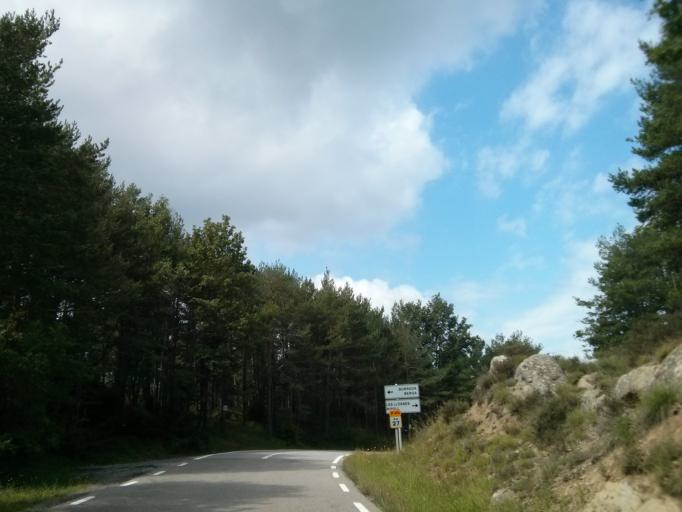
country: ES
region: Catalonia
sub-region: Provincia de Barcelona
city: Borreda
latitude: 42.1385
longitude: 2.0145
